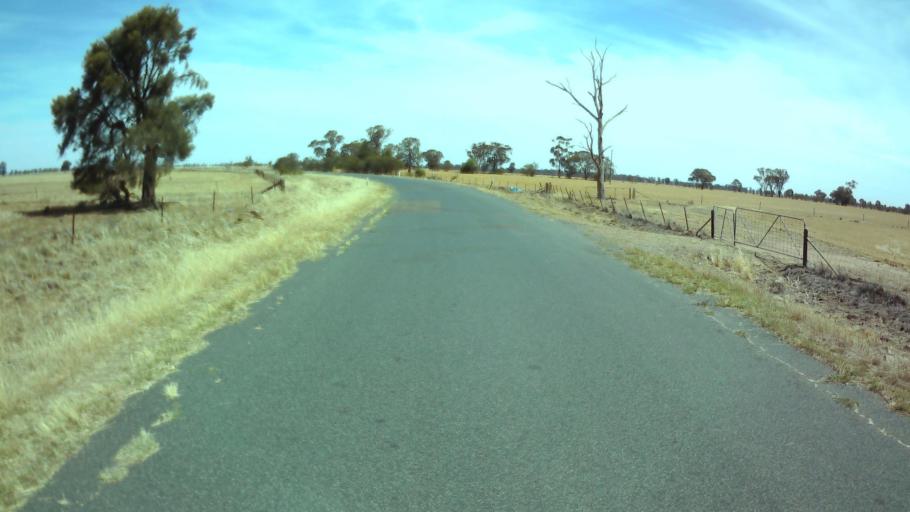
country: AU
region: New South Wales
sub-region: Weddin
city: Grenfell
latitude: -33.9358
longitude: 147.7614
